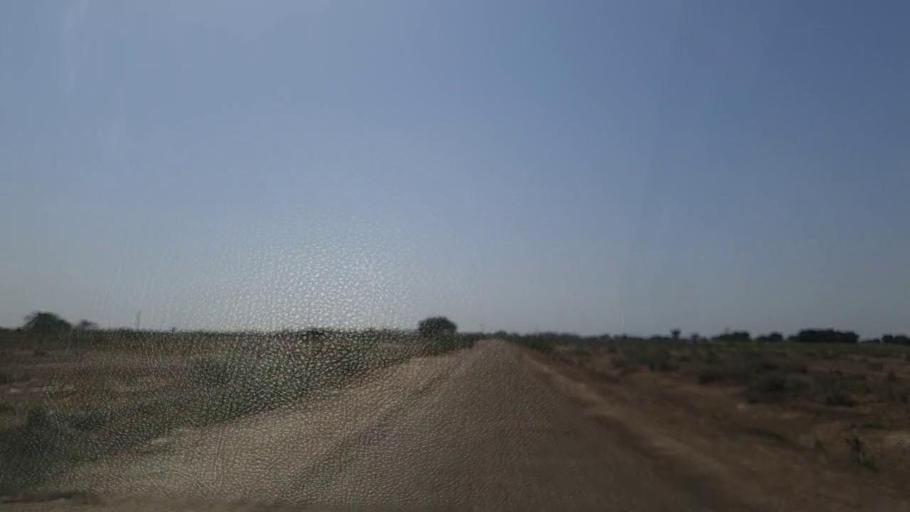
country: PK
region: Sindh
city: Samaro
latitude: 25.2374
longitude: 69.4543
